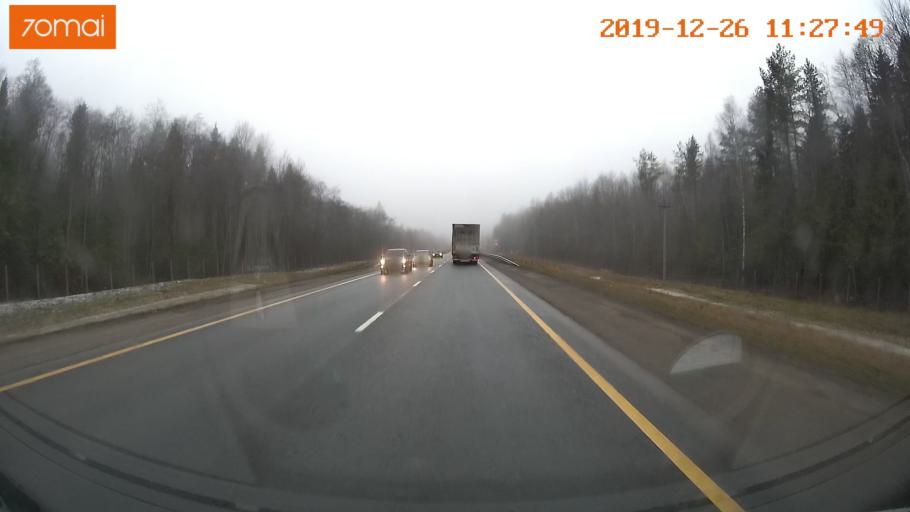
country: RU
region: Vologda
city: Chebsara
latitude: 59.1529
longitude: 38.8280
